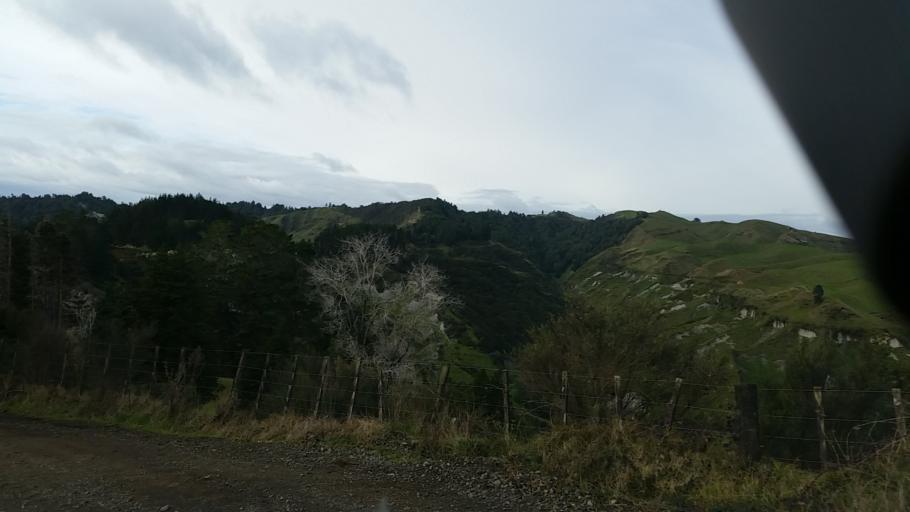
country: NZ
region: Taranaki
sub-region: New Plymouth District
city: Waitara
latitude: -39.0408
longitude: 174.4141
